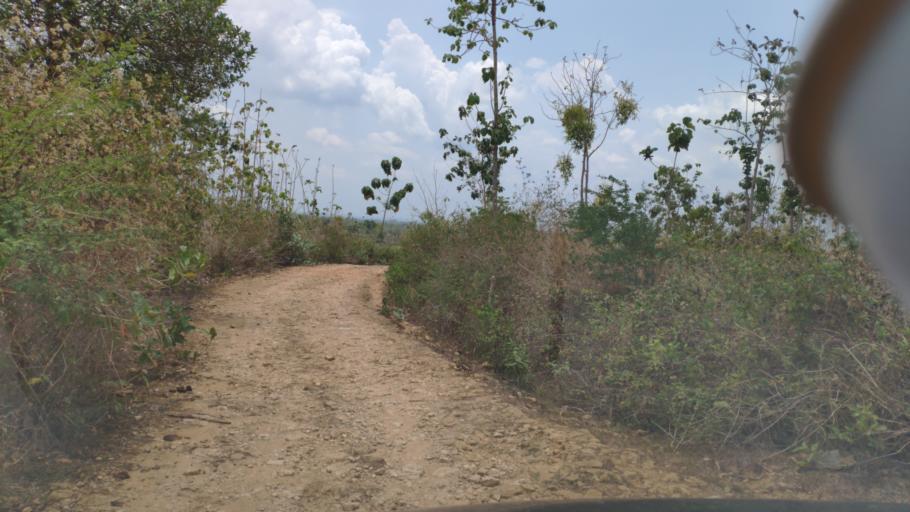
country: ID
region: Central Java
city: Ngapus
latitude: -6.9602
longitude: 111.2194
